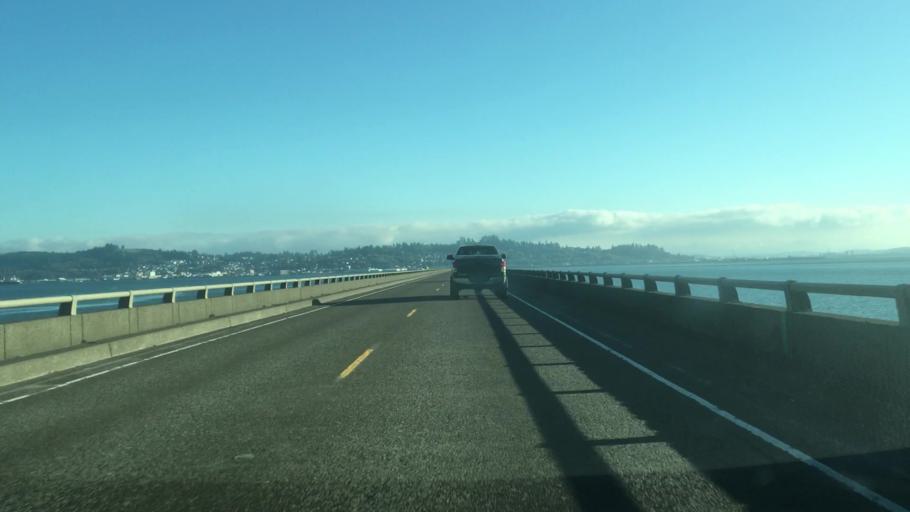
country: US
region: Oregon
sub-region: Clatsop County
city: Astoria
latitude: 46.2204
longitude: -123.8644
